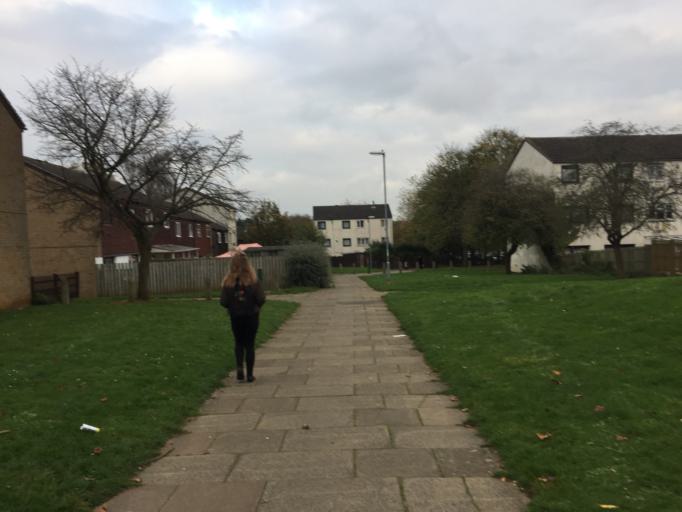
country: GB
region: England
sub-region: Northamptonshire
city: Northampton
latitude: 52.2712
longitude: -0.8425
